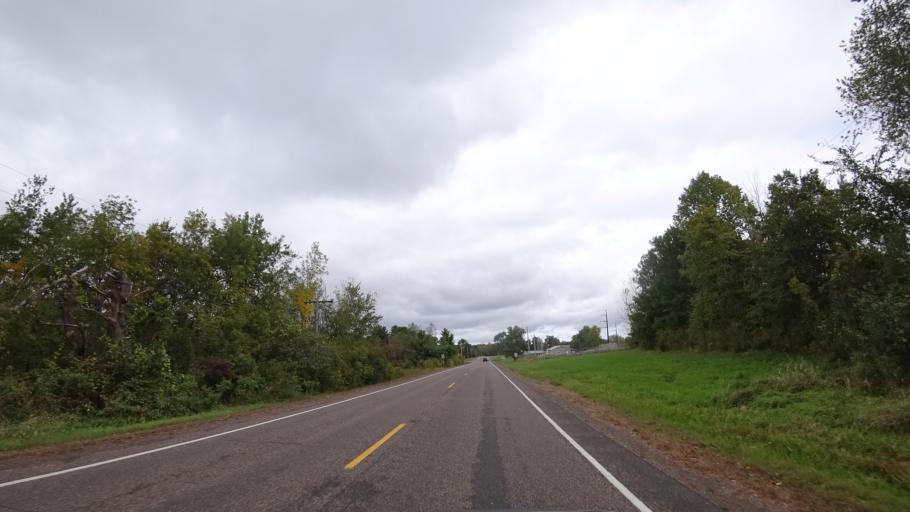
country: US
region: Wisconsin
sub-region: Chippewa County
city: Lake Wissota
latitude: 45.0267
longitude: -91.2870
